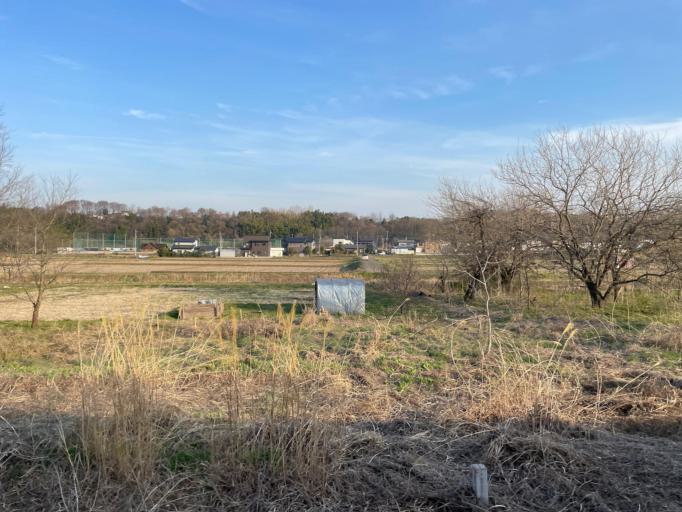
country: JP
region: Gunma
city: Annaka
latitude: 36.3214
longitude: 138.8966
